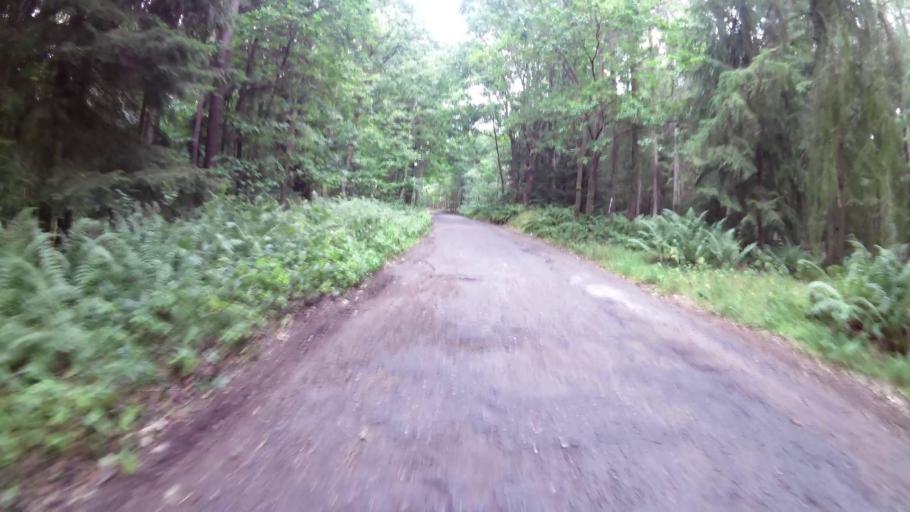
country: PL
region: West Pomeranian Voivodeship
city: Trzcinsko Zdroj
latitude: 52.8971
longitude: 14.6929
